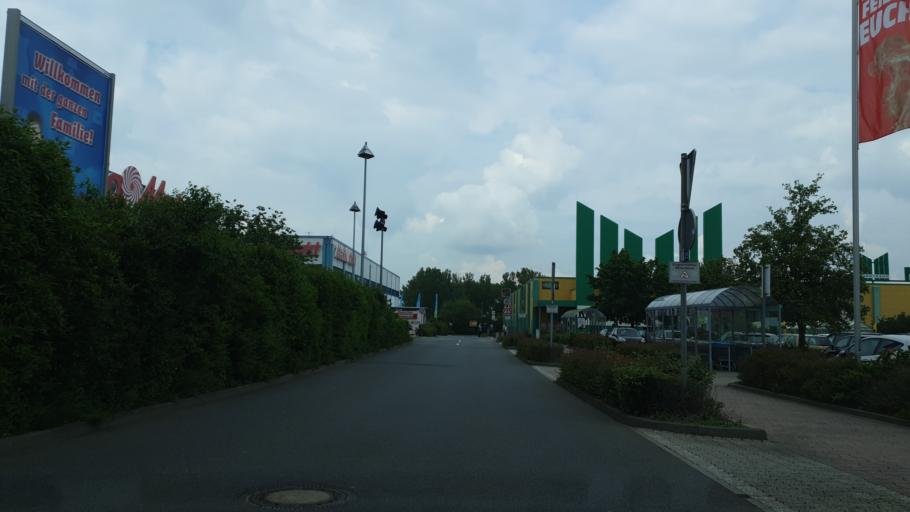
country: DE
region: Saxony
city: Wittgensdorf
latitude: 50.8643
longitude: 12.8676
